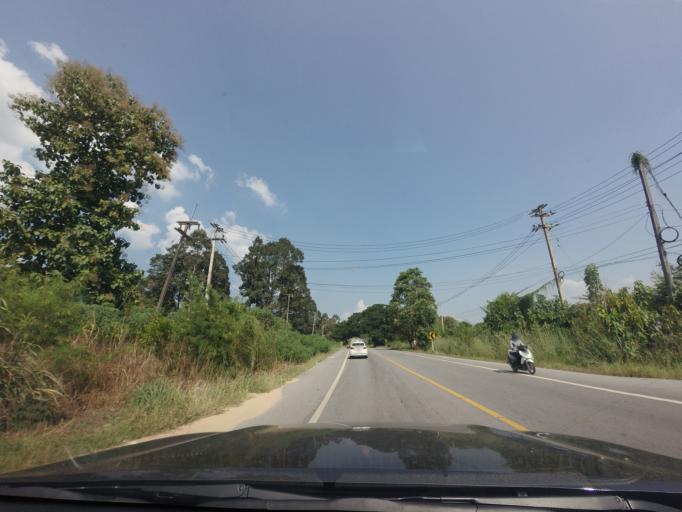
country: TH
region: Phitsanulok
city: Nakhon Thai
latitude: 17.1267
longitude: 100.7447
